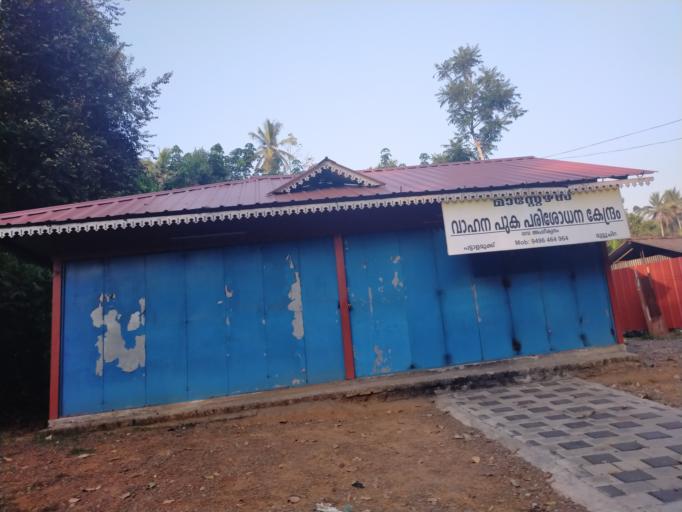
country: IN
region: Kerala
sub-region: Kottayam
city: Vaikam
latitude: 9.7514
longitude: 76.5056
